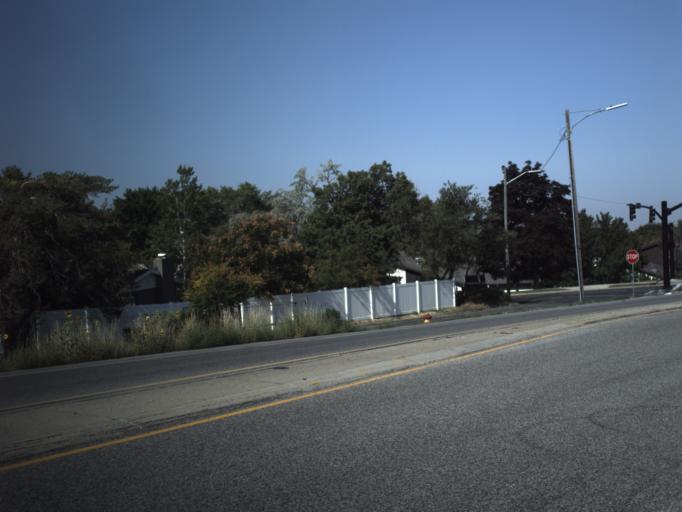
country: US
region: Utah
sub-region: Salt Lake County
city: Canyon Rim
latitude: 40.7183
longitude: -111.8132
